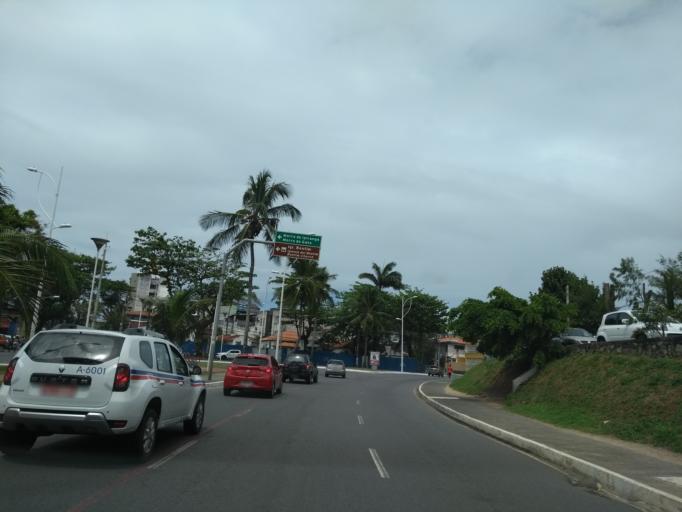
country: BR
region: Bahia
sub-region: Salvador
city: Salvador
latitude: -13.0079
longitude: -38.5236
